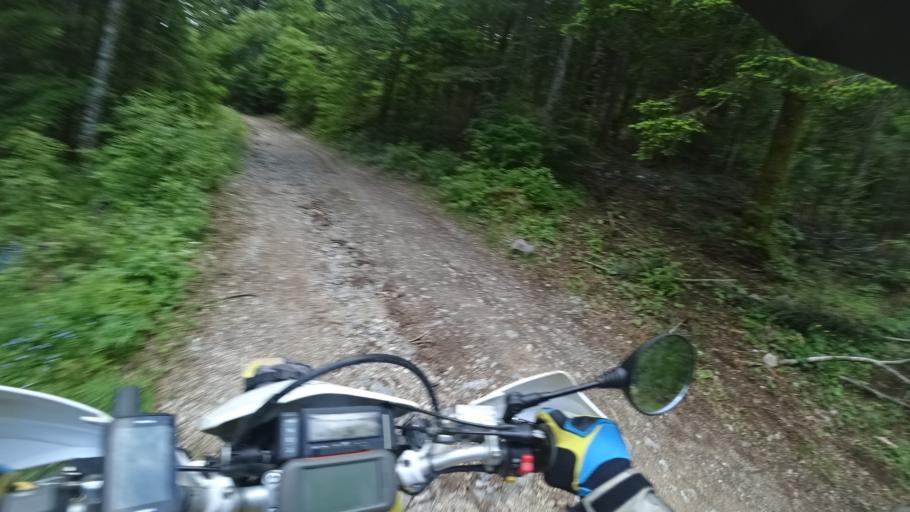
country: HR
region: Zadarska
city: Gracac
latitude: 44.4854
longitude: 15.8780
